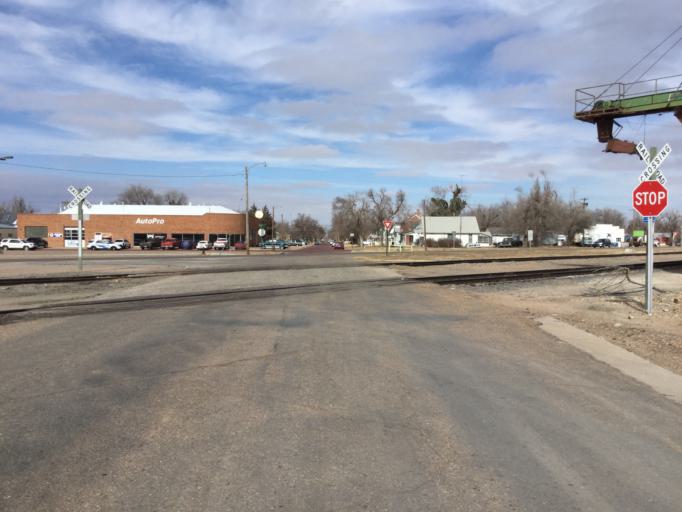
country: US
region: Kansas
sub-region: Pawnee County
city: Larned
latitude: 38.1788
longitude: -99.0956
